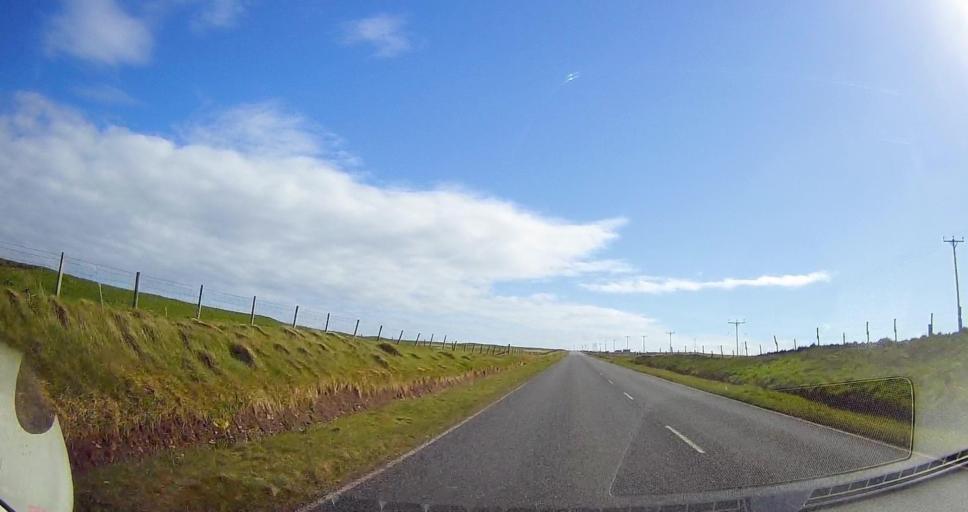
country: GB
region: Scotland
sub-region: Shetland Islands
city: Sandwick
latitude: 59.9044
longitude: -1.3026
